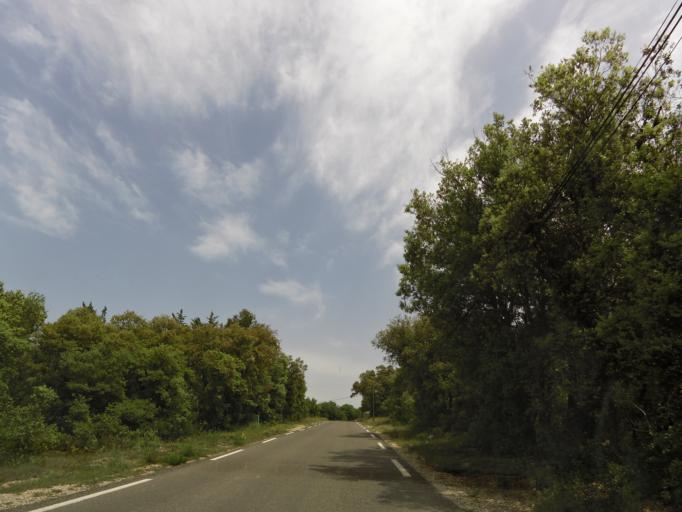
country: FR
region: Languedoc-Roussillon
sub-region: Departement du Gard
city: Aubais
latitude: 43.7627
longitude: 4.1191
